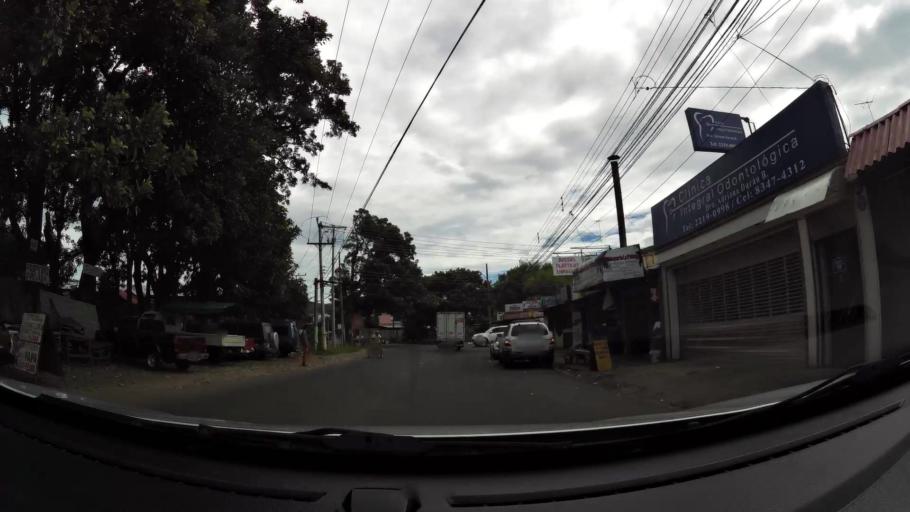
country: CR
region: San Jose
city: Patarra
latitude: 9.8928
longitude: -84.0536
